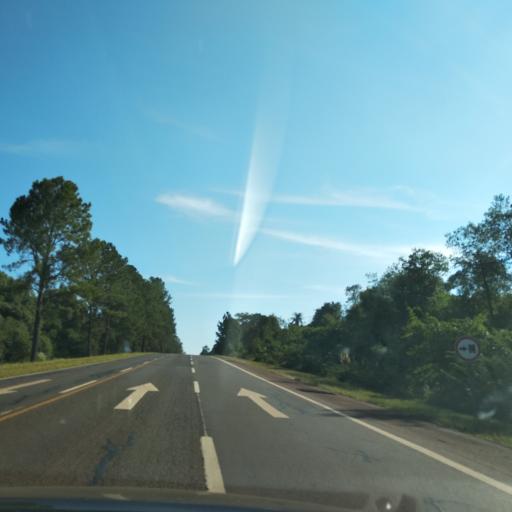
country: AR
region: Misiones
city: Santo Pipo
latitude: -27.1222
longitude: -55.3765
